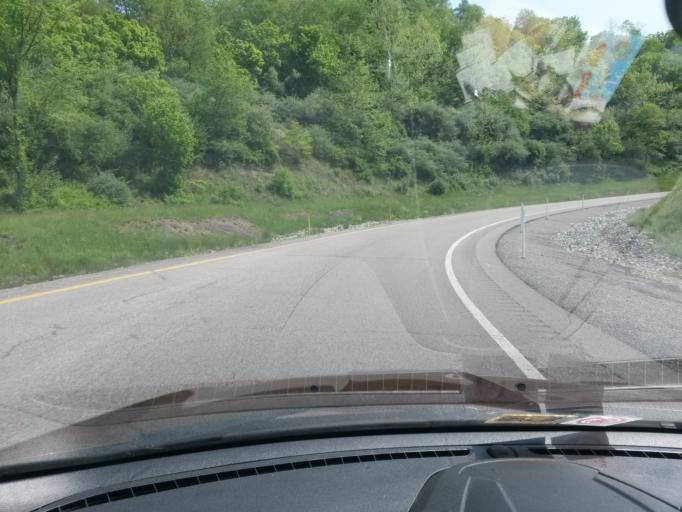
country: US
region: West Virginia
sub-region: Lewis County
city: Weston
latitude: 39.0235
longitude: -80.4287
